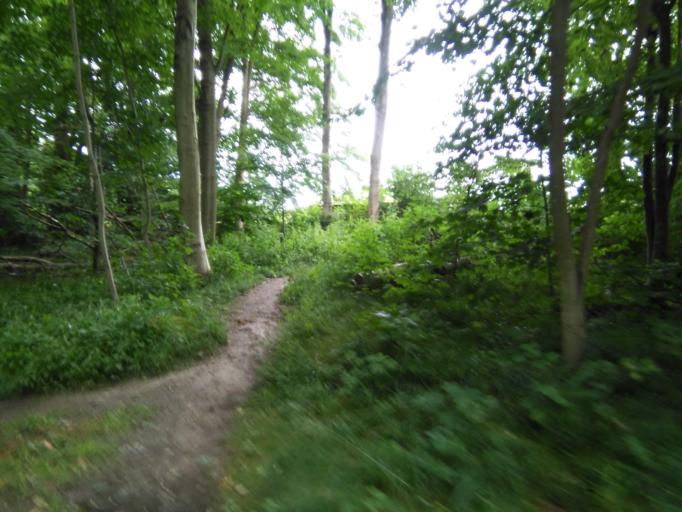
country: DK
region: Central Jutland
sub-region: Arhus Kommune
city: Beder
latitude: 56.0882
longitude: 10.2034
